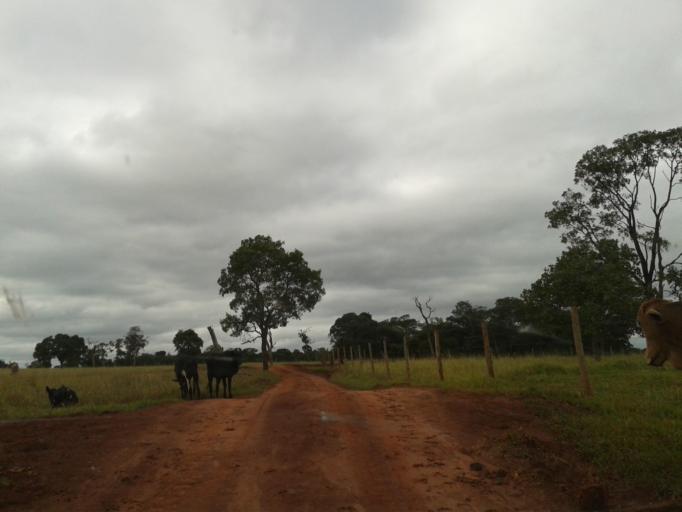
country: BR
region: Minas Gerais
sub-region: Campina Verde
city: Campina Verde
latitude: -19.5023
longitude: -49.6627
